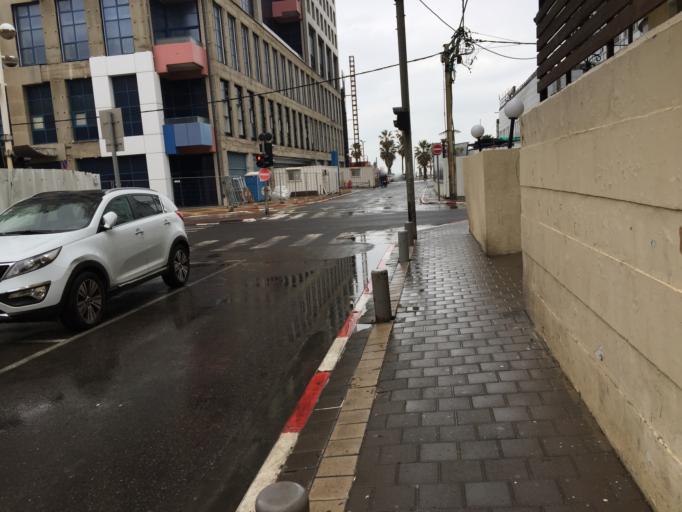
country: IL
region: Tel Aviv
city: Tel Aviv
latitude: 32.0741
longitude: 34.7667
